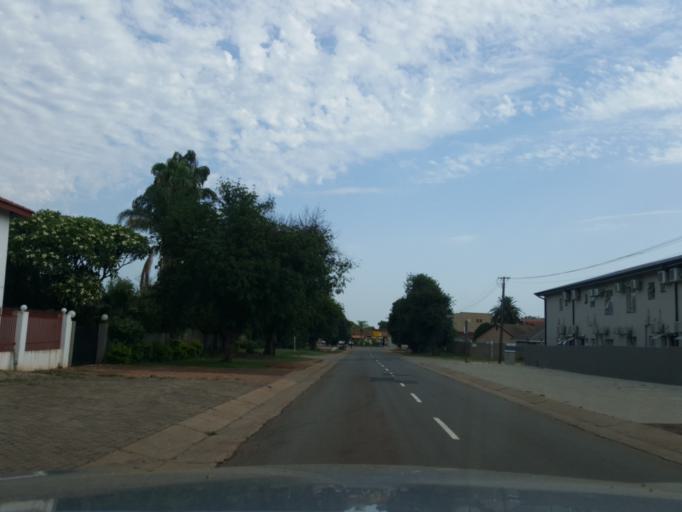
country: SZ
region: Hhohho
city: Ntfonjeni
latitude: -25.4967
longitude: 31.5089
